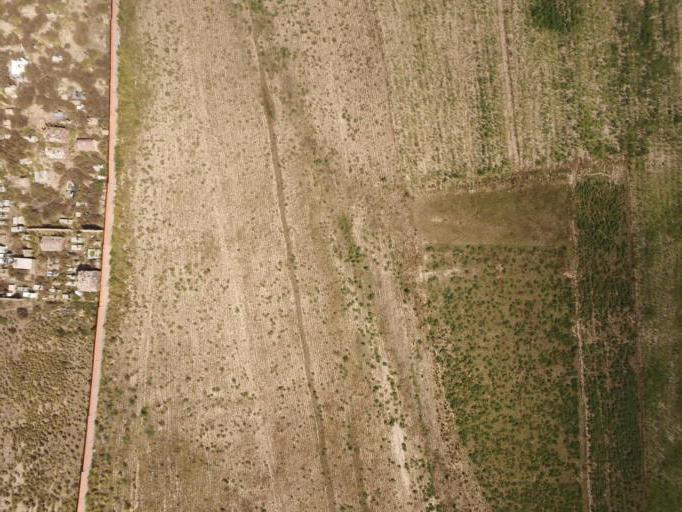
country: BO
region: Oruro
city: Challapata
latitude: -18.6920
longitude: -66.7612
